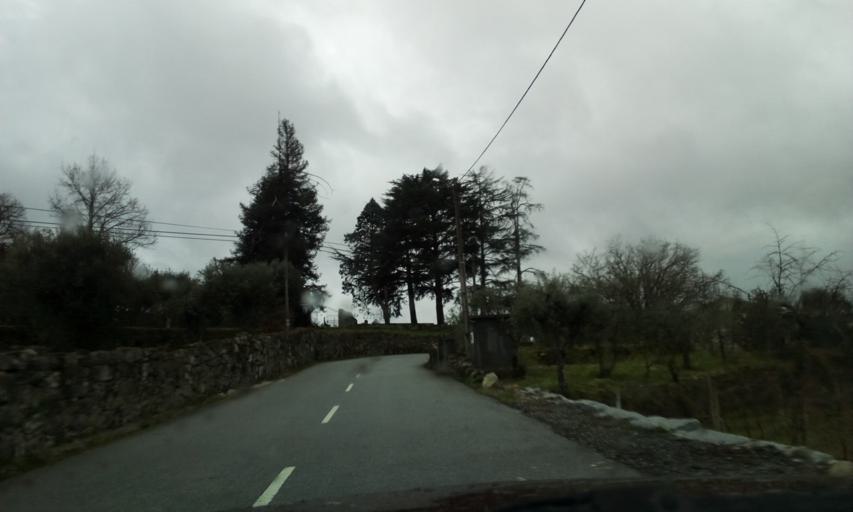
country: PT
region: Viseu
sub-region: Mangualde
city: Mangualde
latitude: 40.6108
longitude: -7.8148
